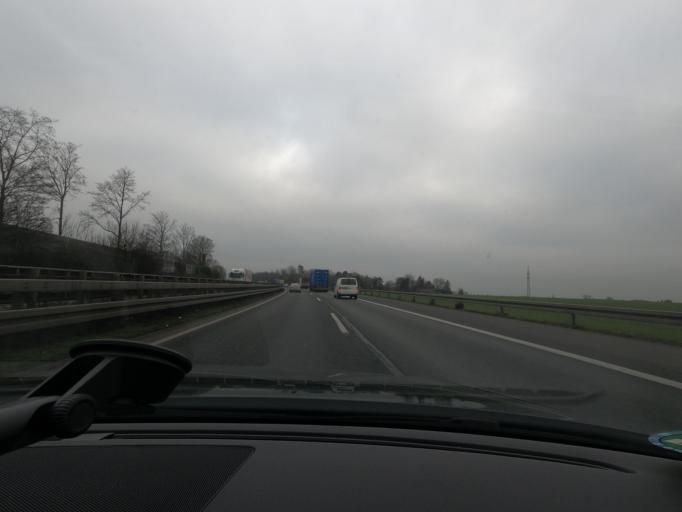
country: DE
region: North Rhine-Westphalia
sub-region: Regierungsbezirk Dusseldorf
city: Monchengladbach
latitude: 51.1368
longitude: 6.4247
